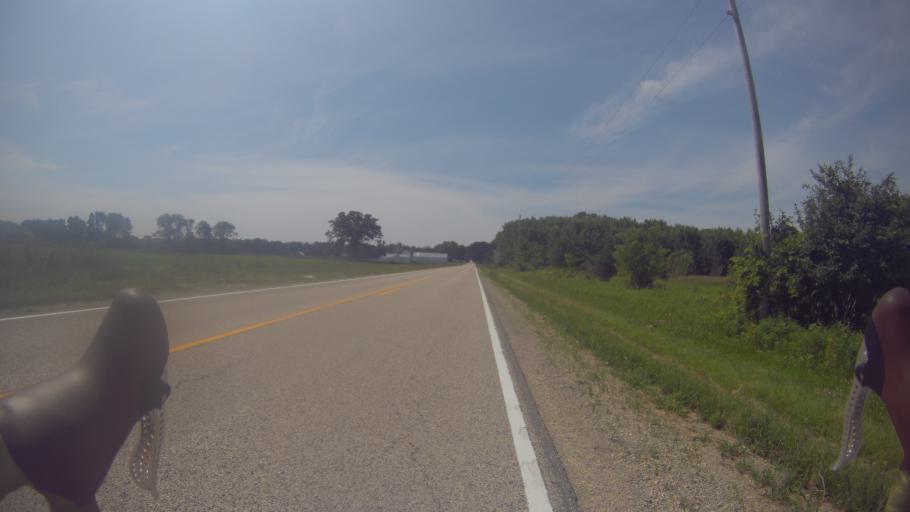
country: US
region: Wisconsin
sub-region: Jefferson County
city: Cambridge
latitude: 43.0542
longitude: -89.0115
